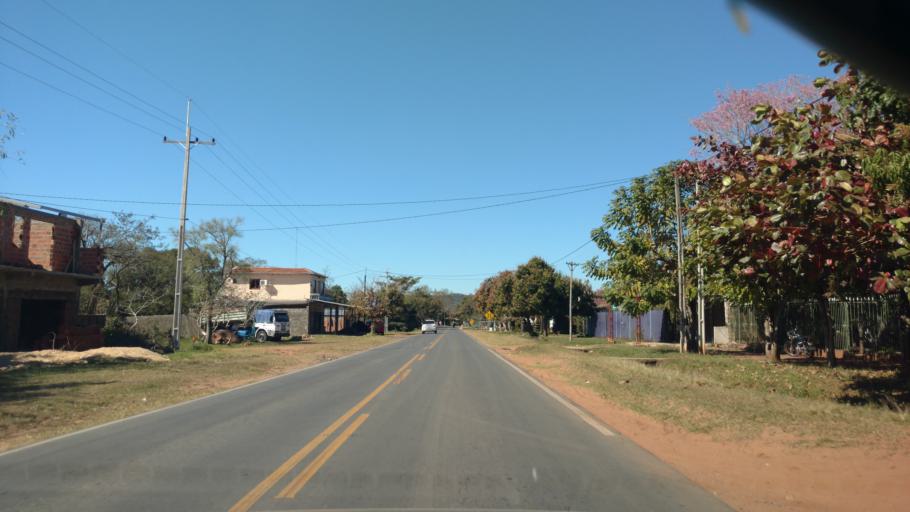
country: PY
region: Paraguari
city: Pirayu
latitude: -25.4556
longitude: -57.2721
